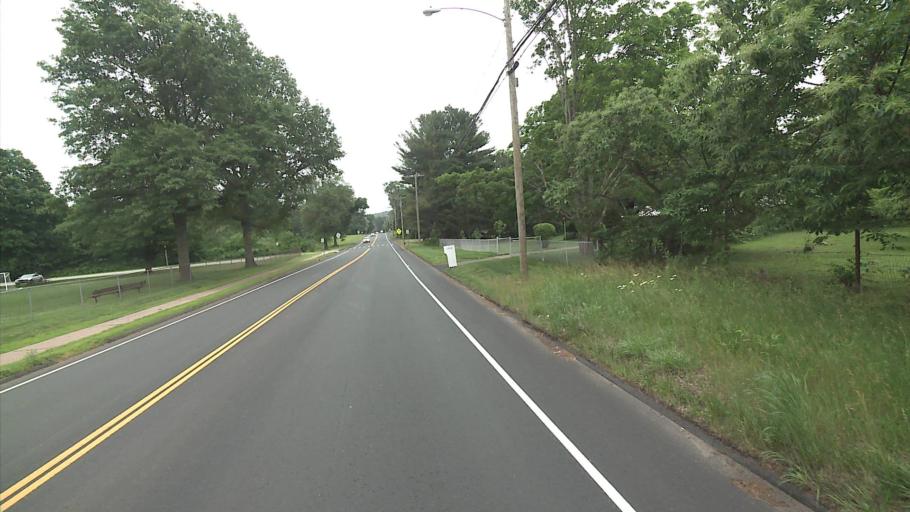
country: US
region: Connecticut
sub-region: Hartford County
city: Glastonbury Center
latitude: 41.7174
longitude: -72.5594
